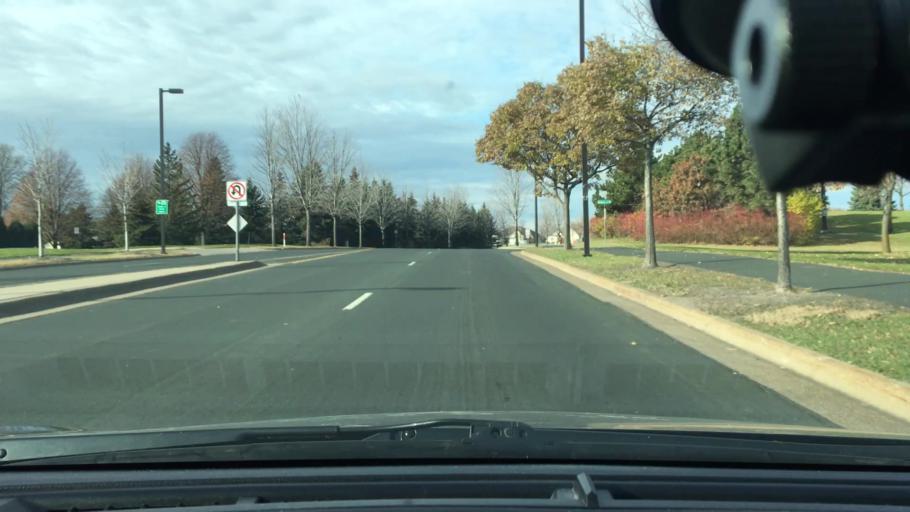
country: US
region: Minnesota
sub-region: Hennepin County
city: Maple Grove
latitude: 45.1026
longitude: -93.4707
